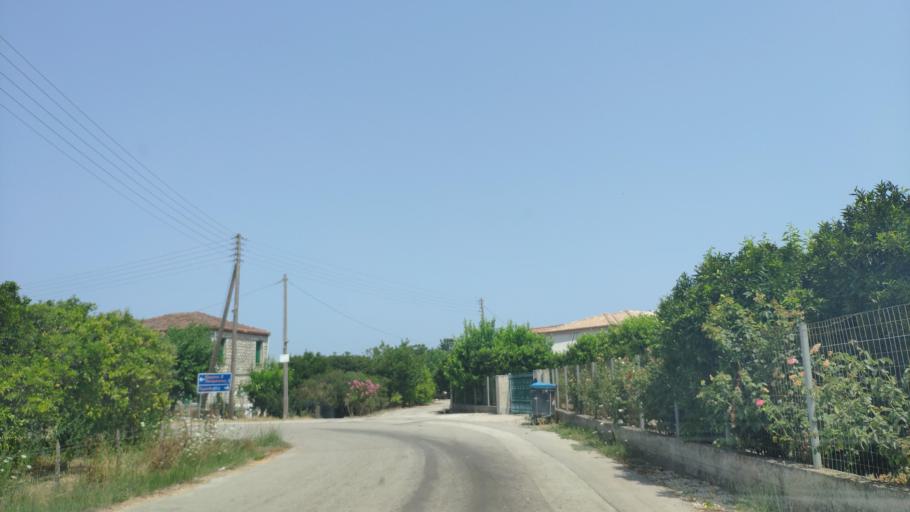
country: GR
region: Epirus
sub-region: Nomos Artas
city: Neochori
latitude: 39.0620
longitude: 21.0559
